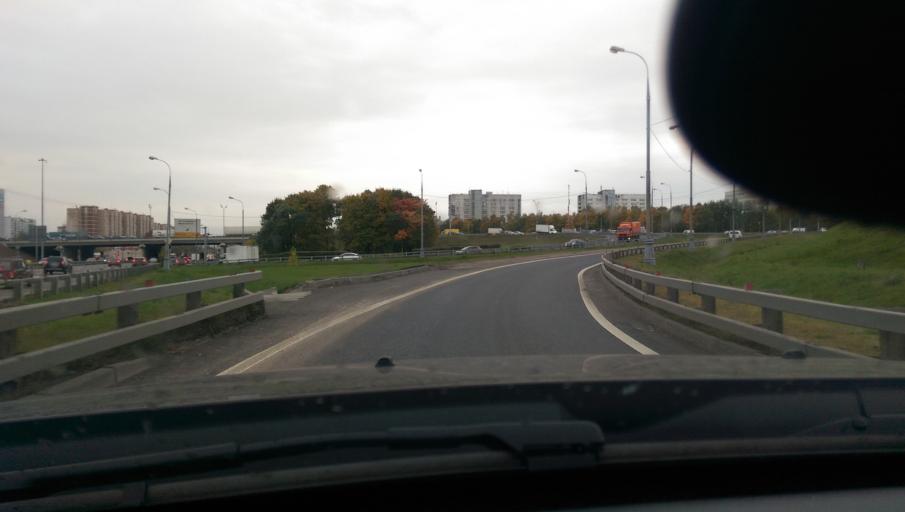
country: RU
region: Moscow
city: Vatutino
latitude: 55.8973
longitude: 37.6722
